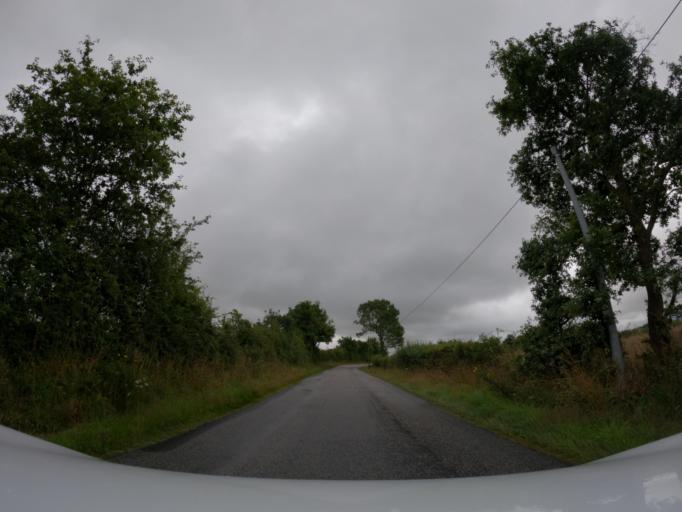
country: FR
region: Pays de la Loire
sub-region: Departement de la Loire-Atlantique
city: Saint-Mars-du-Desert
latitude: 47.3775
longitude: -1.4198
